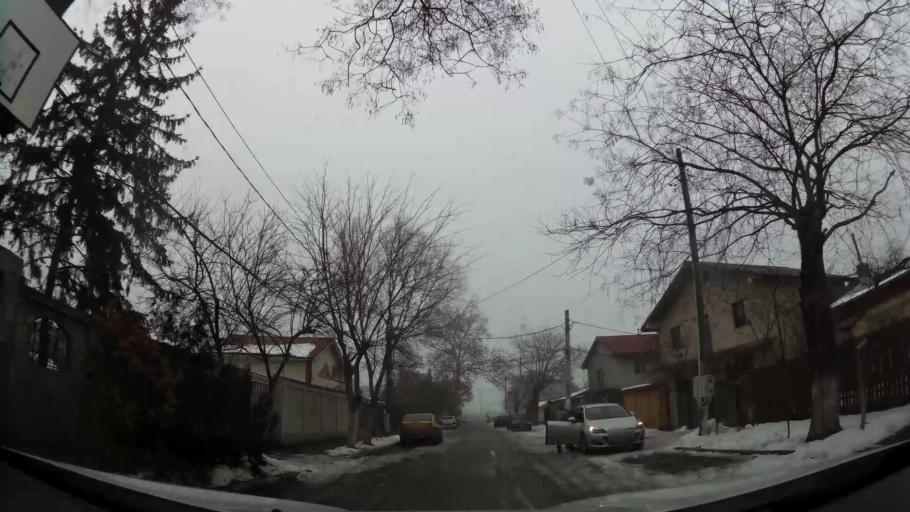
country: RO
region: Ilfov
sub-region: Comuna Chiajna
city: Rosu
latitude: 44.4508
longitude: 26.0103
